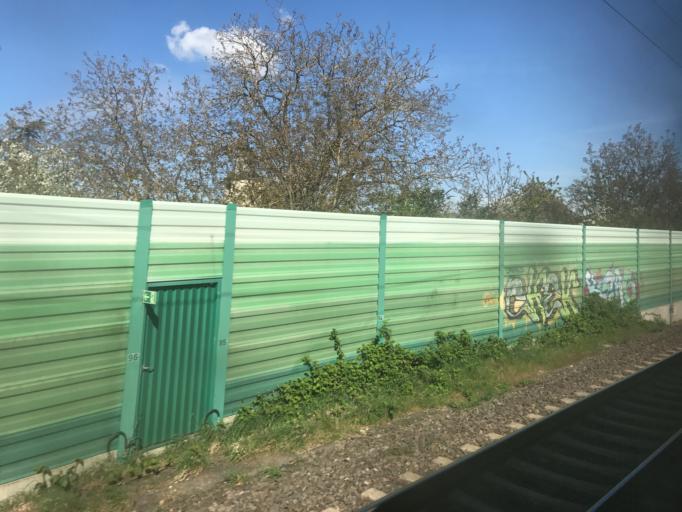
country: DE
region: Rheinland-Pfalz
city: Dienheim
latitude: 49.8368
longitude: 8.3562
